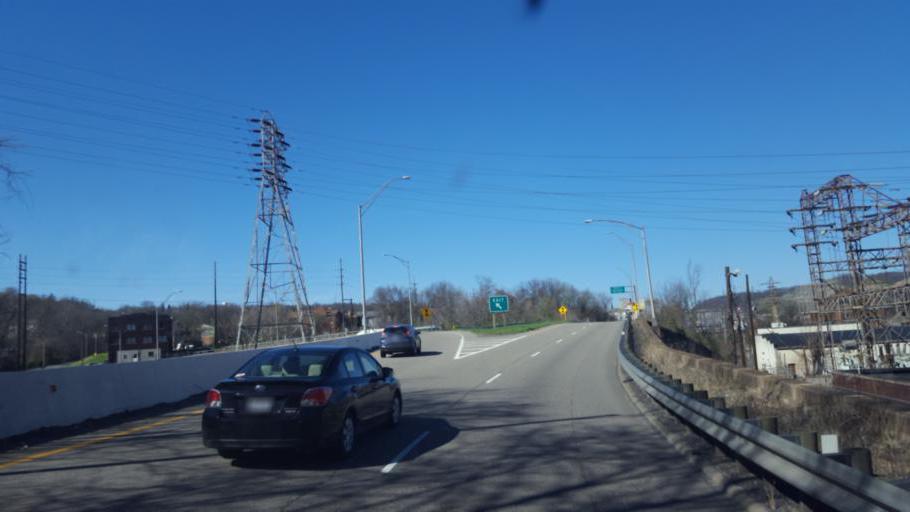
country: US
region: Ohio
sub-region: Jefferson County
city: Steubenville
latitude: 40.3502
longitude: -80.6191
